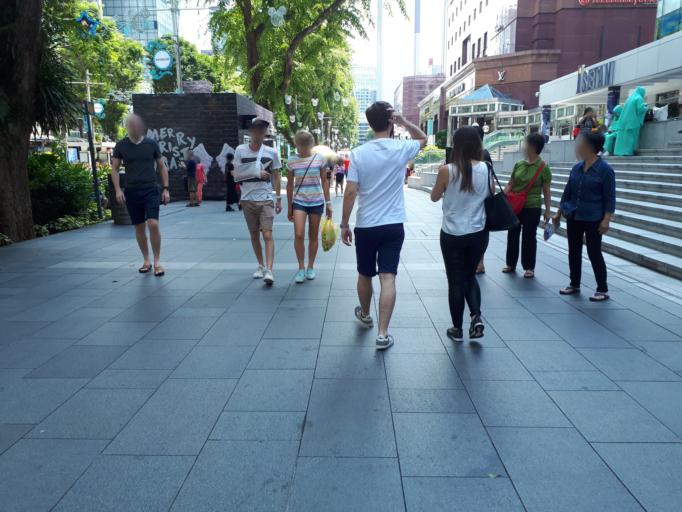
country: SG
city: Singapore
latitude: 1.3041
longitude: 103.8339
